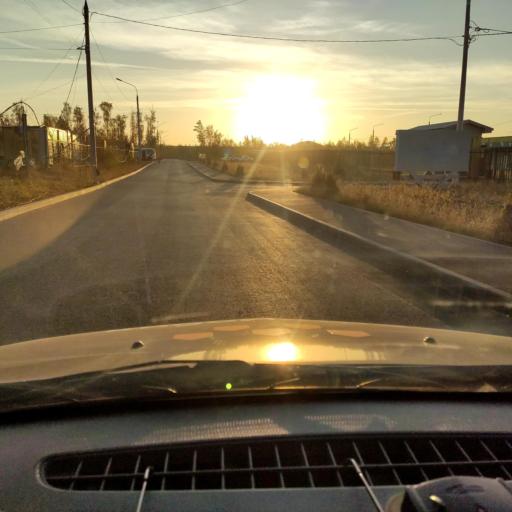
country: RU
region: Voronezj
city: Maslovka
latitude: 51.5882
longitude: 39.2422
